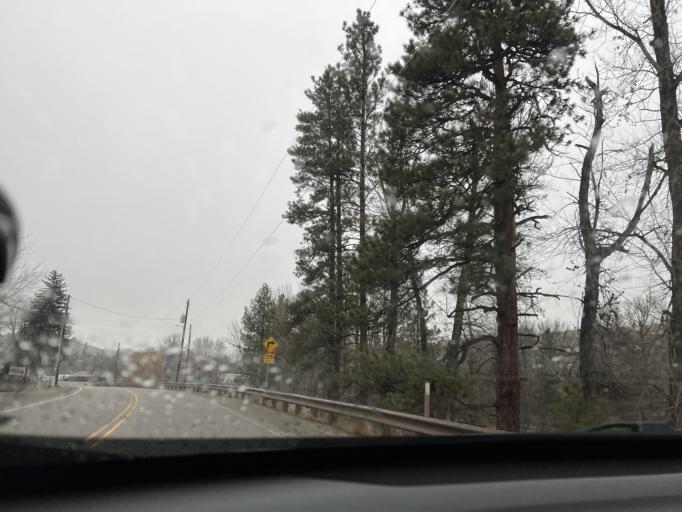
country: US
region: Washington
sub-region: Okanogan County
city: Brewster
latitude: 48.4704
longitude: -120.1779
